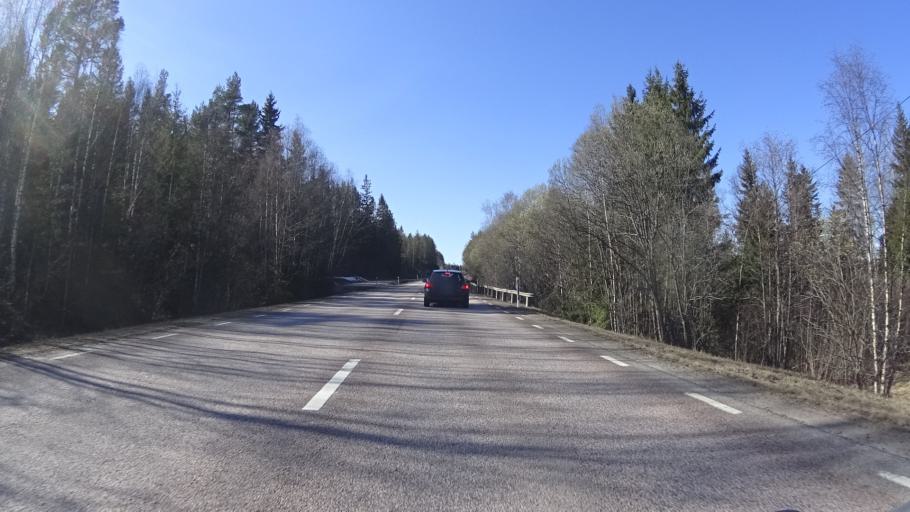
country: SE
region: Vaermland
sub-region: Karlstads Kommun
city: Edsvalla
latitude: 59.5418
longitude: 13.0820
